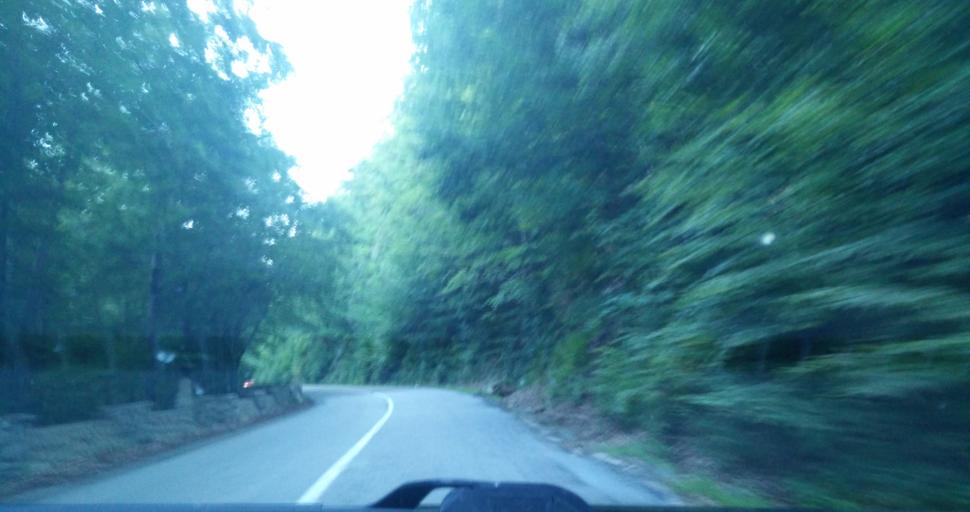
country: RO
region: Bihor
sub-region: Oras Nucet
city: Nucet
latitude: 46.4842
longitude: 22.6021
